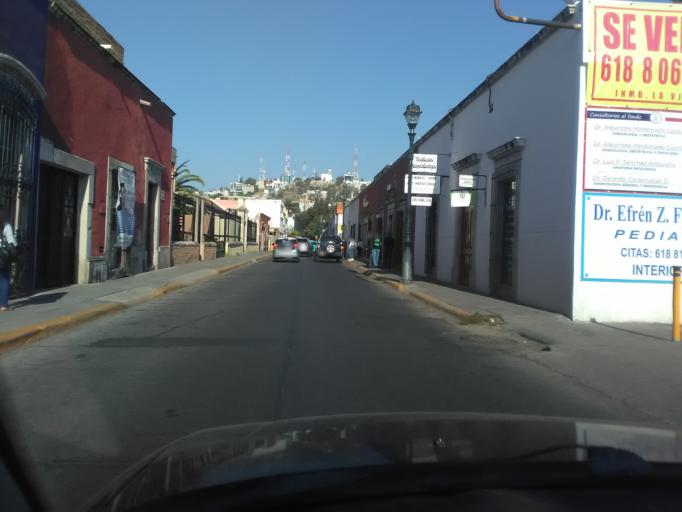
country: MX
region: Durango
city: Victoria de Durango
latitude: 24.0226
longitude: -104.6748
